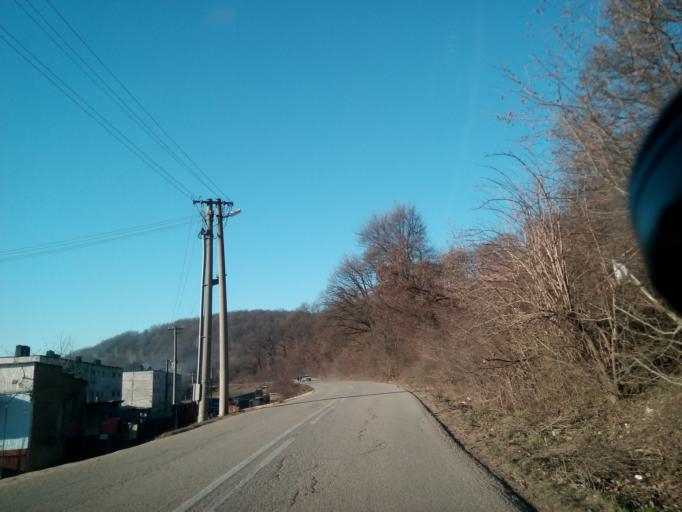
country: SK
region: Kosicky
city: Medzev
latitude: 48.6895
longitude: 20.9642
